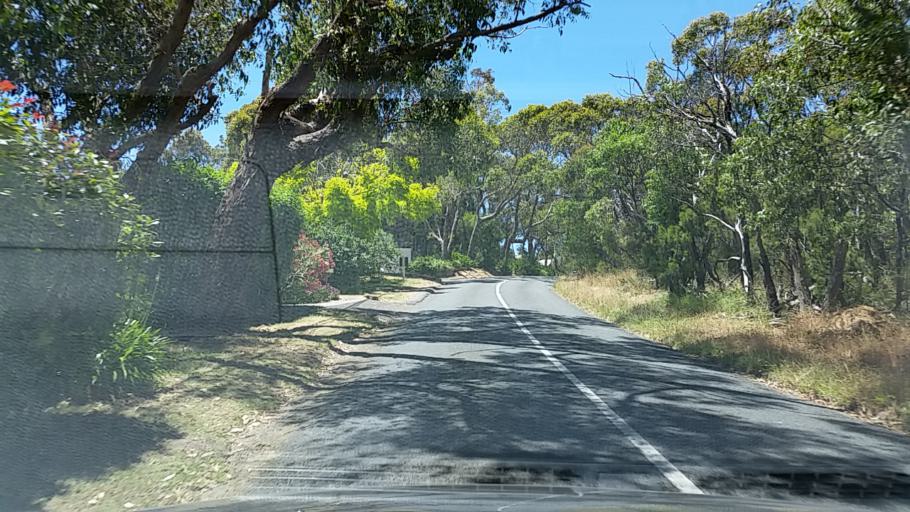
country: AU
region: South Australia
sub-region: Adelaide Hills
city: Crafers
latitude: -34.9901
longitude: 138.6824
